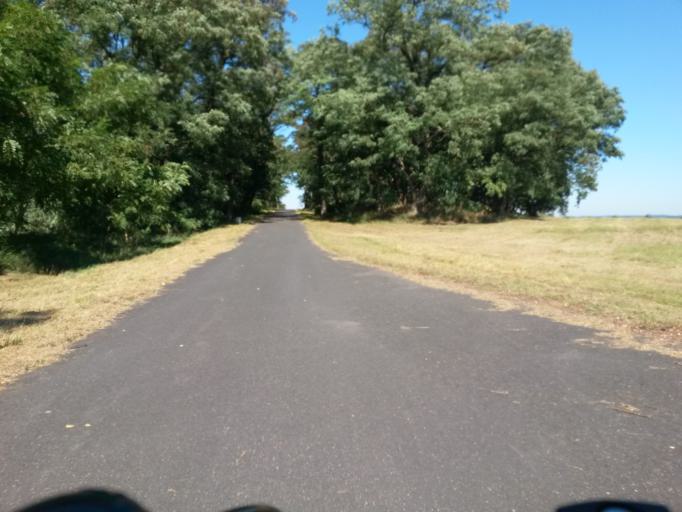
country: PL
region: West Pomeranian Voivodeship
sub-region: Powiat gryfinski
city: Cedynia
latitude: 52.8859
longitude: 14.1577
